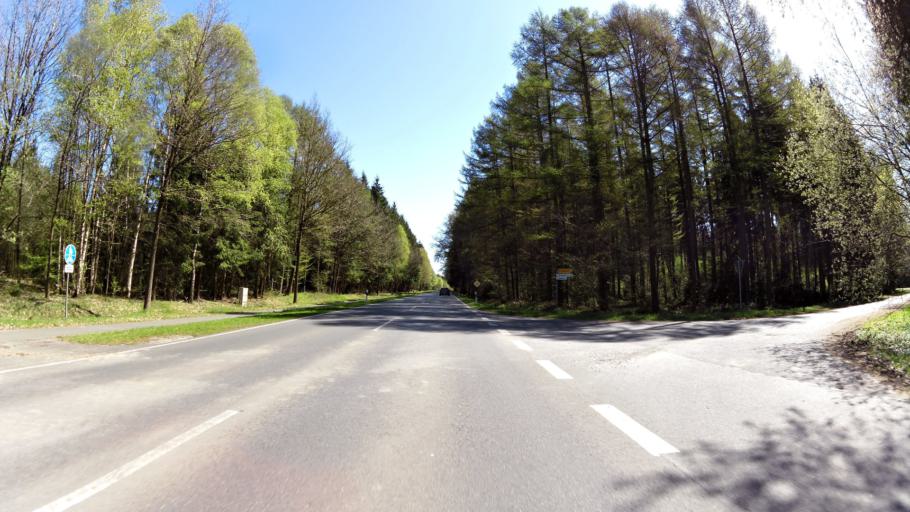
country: DE
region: Lower Saxony
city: Soltau
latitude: 53.0109
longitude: 9.7888
